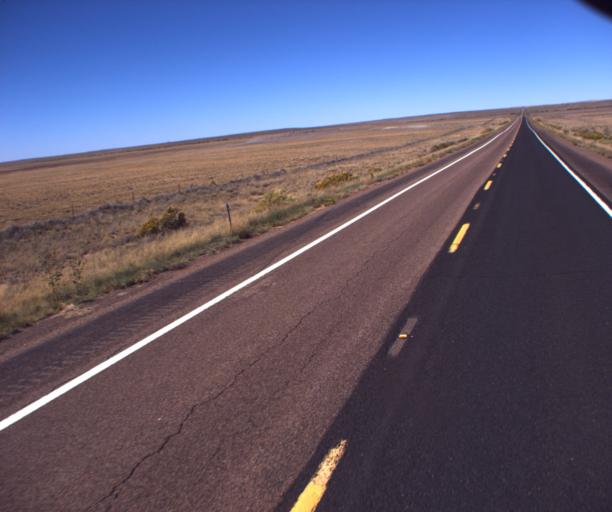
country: US
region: Arizona
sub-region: Navajo County
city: Snowflake
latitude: 34.7232
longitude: -109.7750
